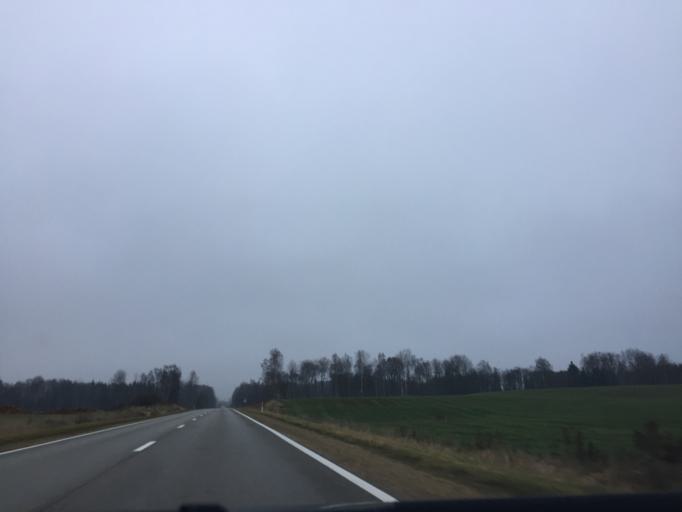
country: LV
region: Pargaujas
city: Stalbe
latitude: 57.4092
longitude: 25.1230
